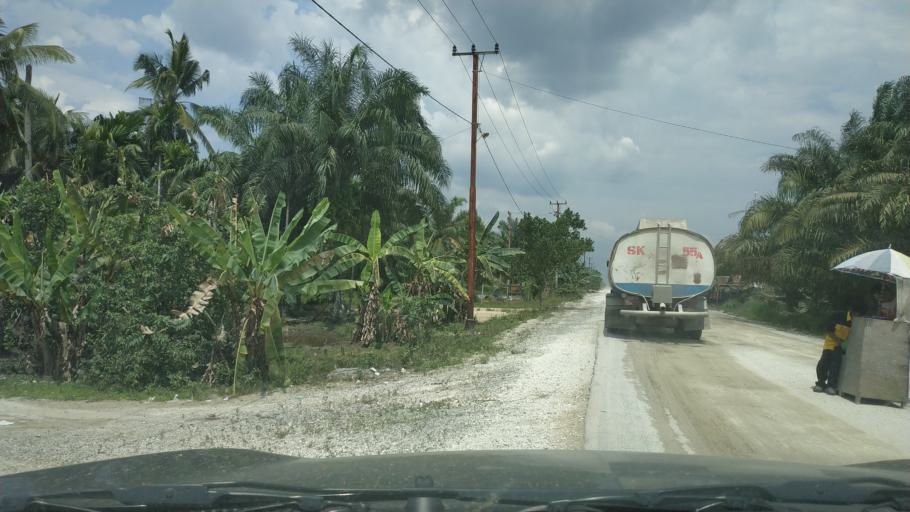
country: ID
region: Riau
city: Sungaisalak
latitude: -0.5986
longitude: 102.9033
